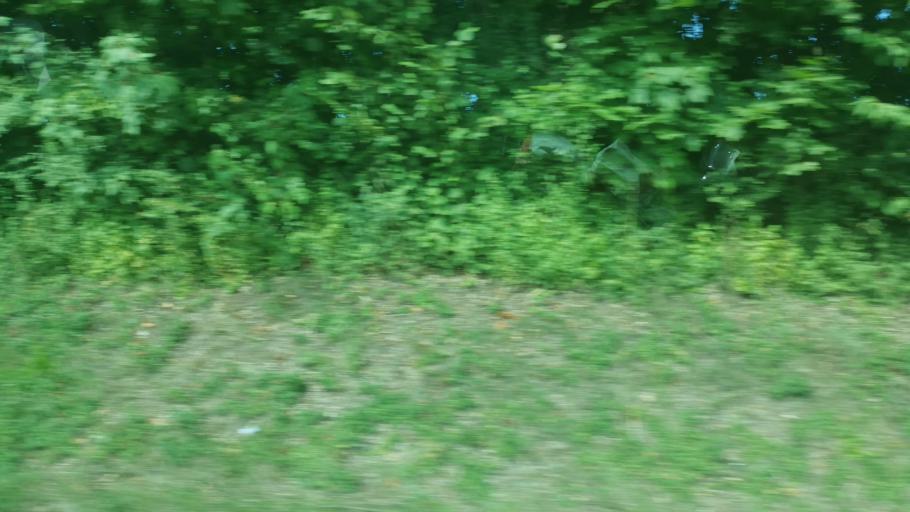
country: DE
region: Bavaria
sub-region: Upper Palatinate
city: Willmering
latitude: 49.2361
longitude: 12.6744
